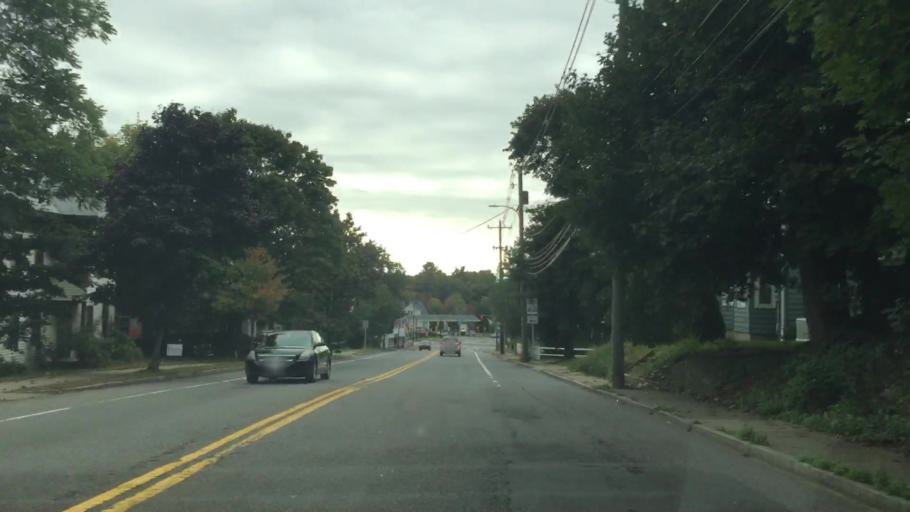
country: US
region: Massachusetts
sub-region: Essex County
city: Middleton
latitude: 42.5966
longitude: -71.0175
